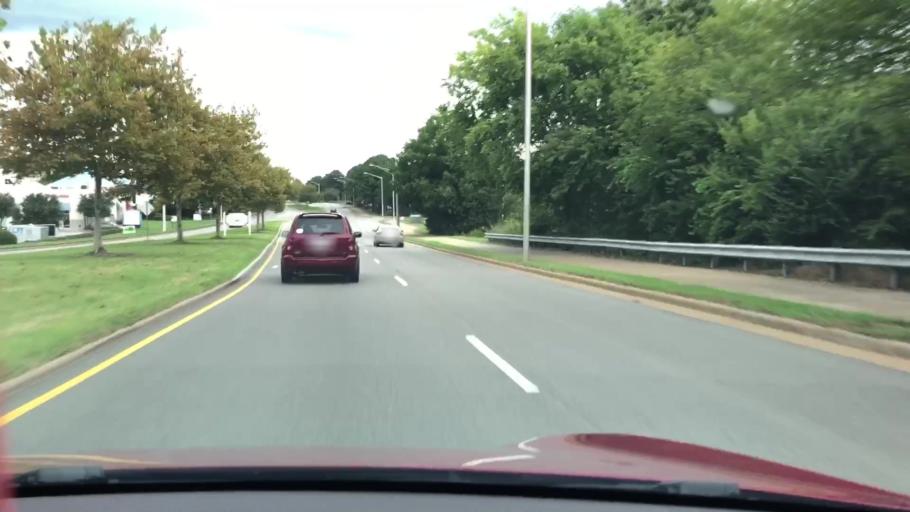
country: US
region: Virginia
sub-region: City of Virginia Beach
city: Virginia Beach
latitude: 36.9061
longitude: -76.0673
